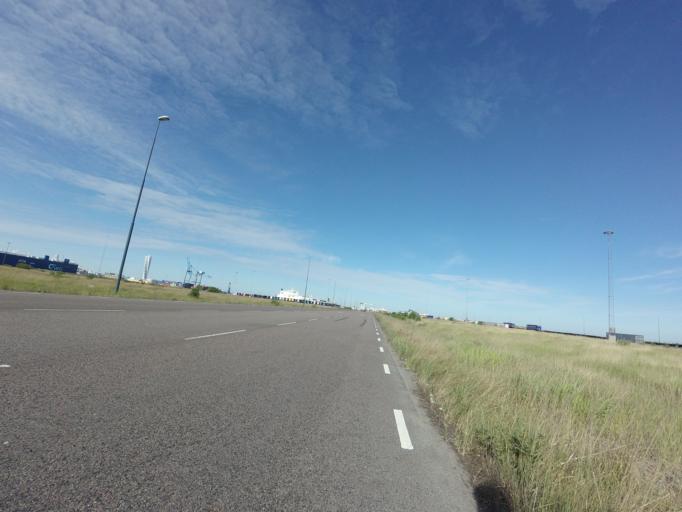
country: SE
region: Skane
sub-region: Malmo
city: Malmoe
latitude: 55.6293
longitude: 13.0002
